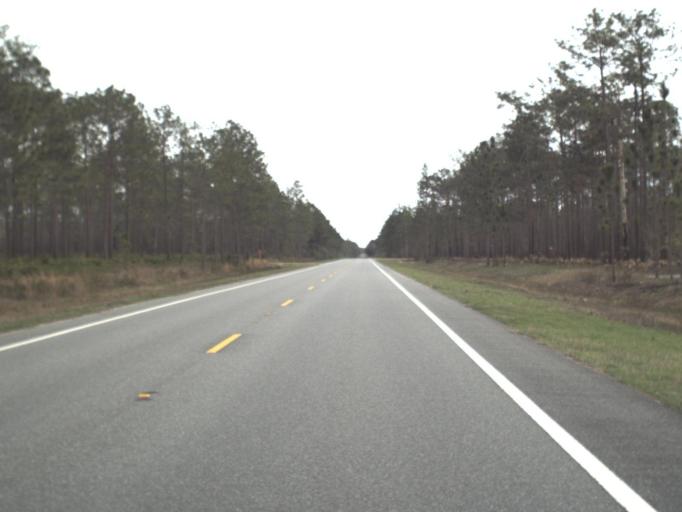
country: US
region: Florida
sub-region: Gadsden County
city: Midway
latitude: 30.3419
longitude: -84.4943
